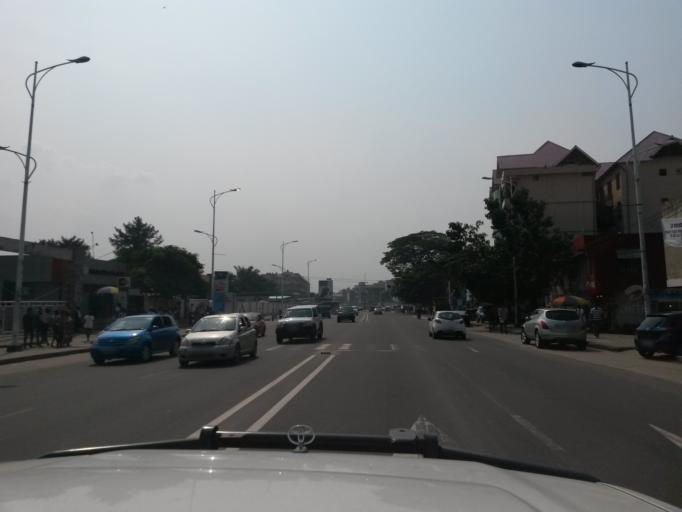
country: CD
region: Kinshasa
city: Kinshasa
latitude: -4.3206
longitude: 15.2943
